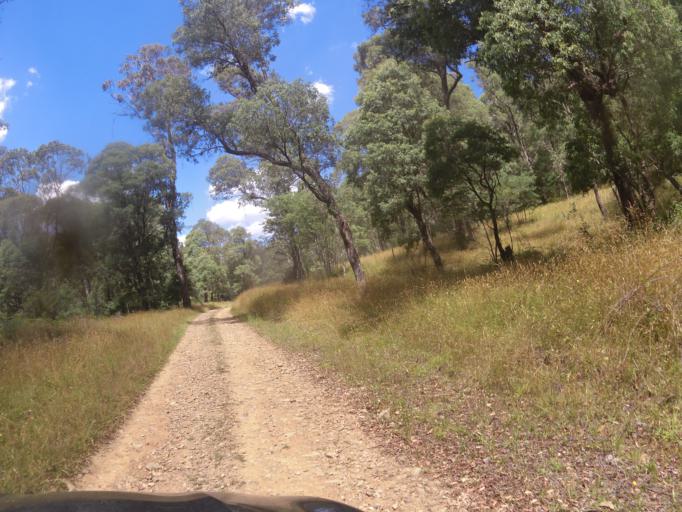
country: AU
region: Victoria
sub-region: Alpine
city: Mount Beauty
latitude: -36.7831
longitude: 147.0744
